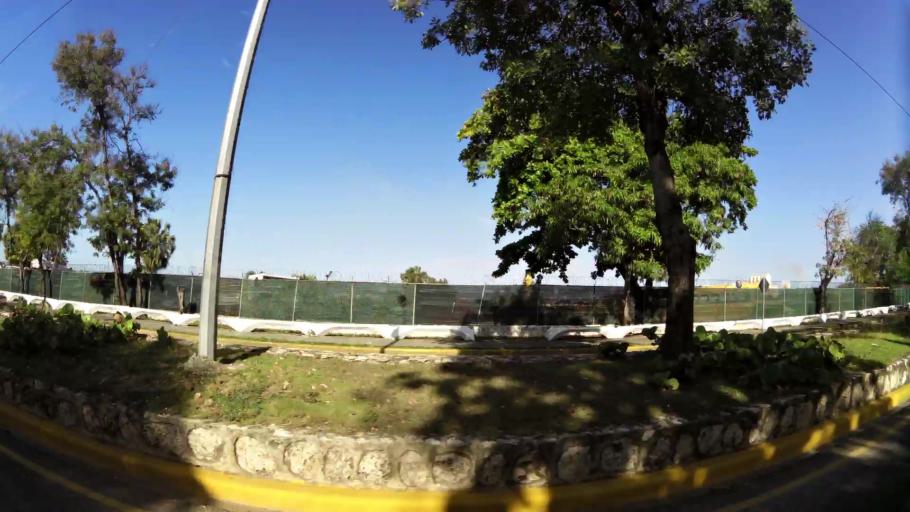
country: DO
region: Nacional
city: Ciudad Nueva
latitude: 18.4692
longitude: -69.8748
